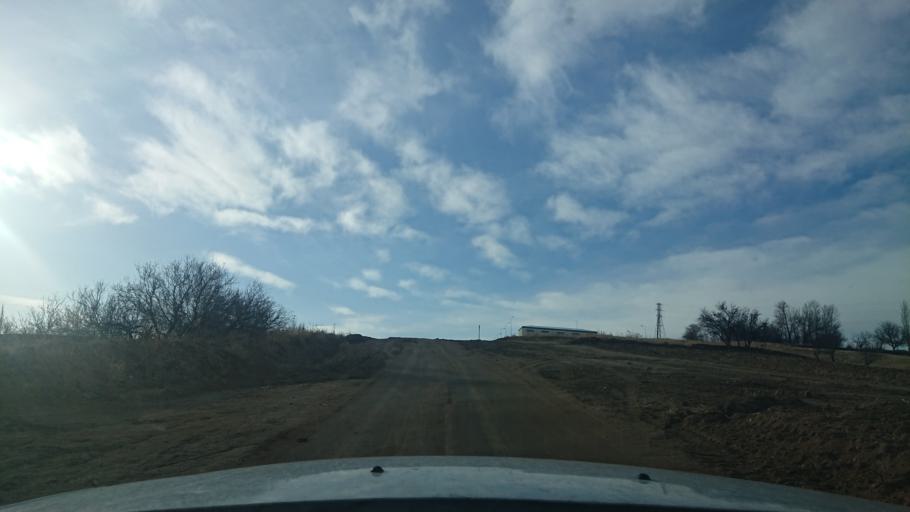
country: TR
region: Aksaray
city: Agacoren
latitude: 38.8554
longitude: 33.9429
